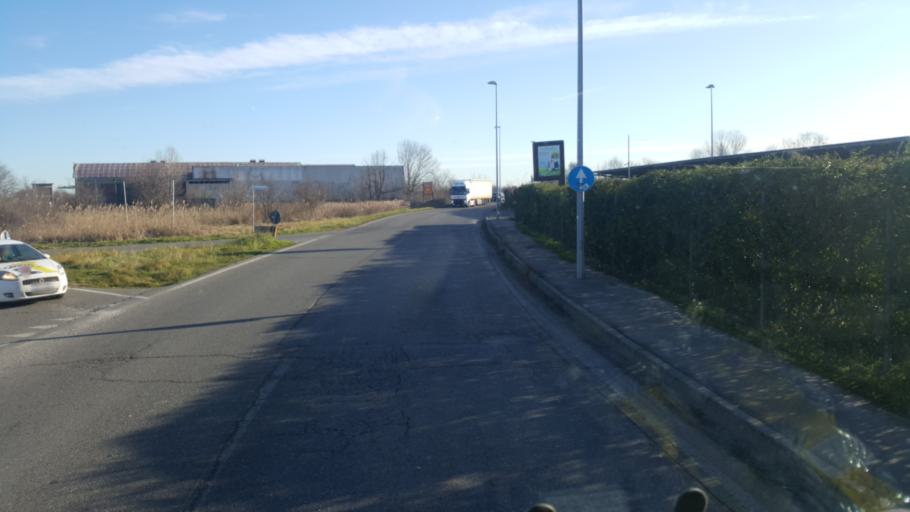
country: IT
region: Emilia-Romagna
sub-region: Provincia di Modena
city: Campogalliano
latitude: 44.6566
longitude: 10.8570
